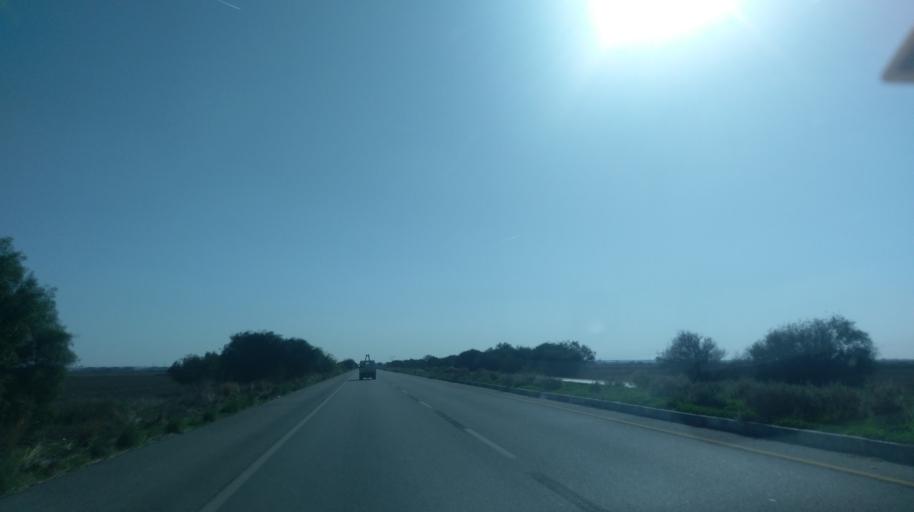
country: CY
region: Ammochostos
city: Acheritou
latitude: 35.1457
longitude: 33.8575
